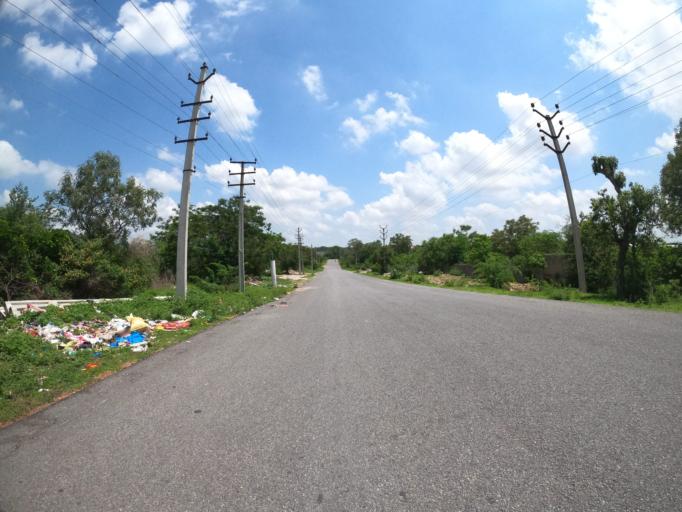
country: IN
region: Telangana
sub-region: Medak
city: Serilingampalle
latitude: 17.3916
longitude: 78.3141
